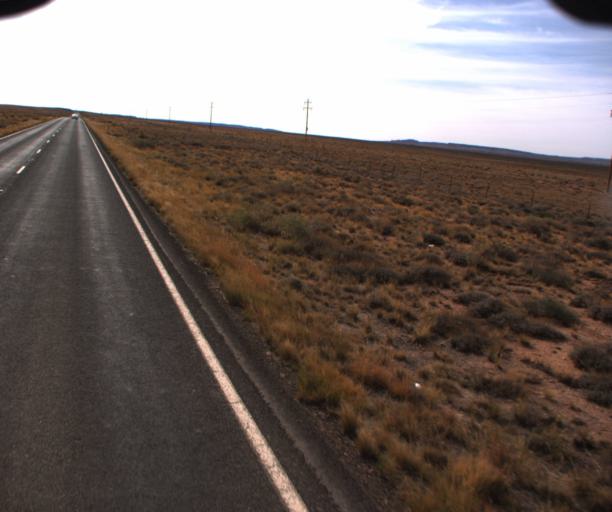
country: US
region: Arizona
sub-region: Apache County
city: Ganado
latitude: 35.8992
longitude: -109.6103
